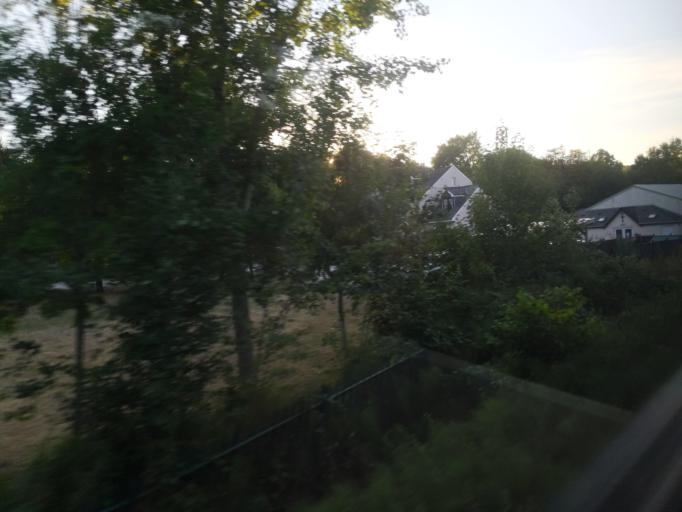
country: GB
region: England
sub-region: Devon
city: Kingskerswell
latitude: 50.4993
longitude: -3.5851
